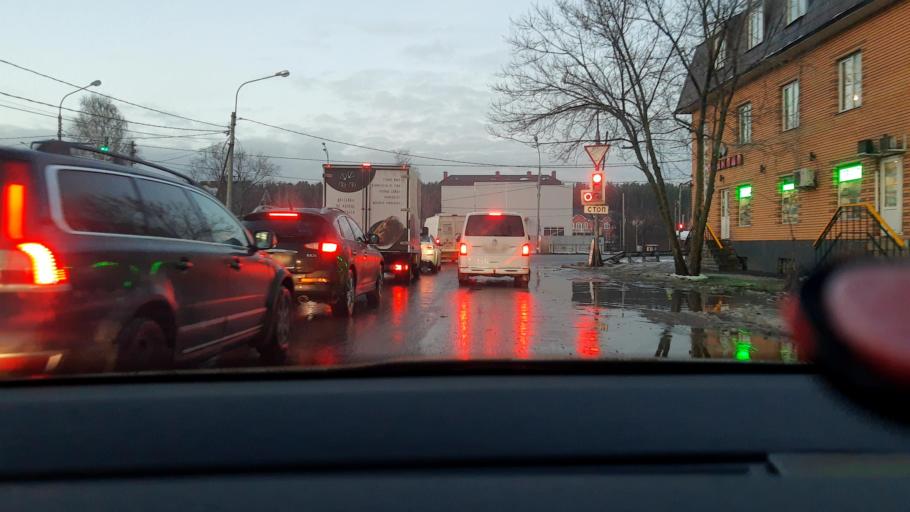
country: RU
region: Moskovskaya
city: Staraya Kupavna
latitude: 55.8186
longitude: 38.1616
